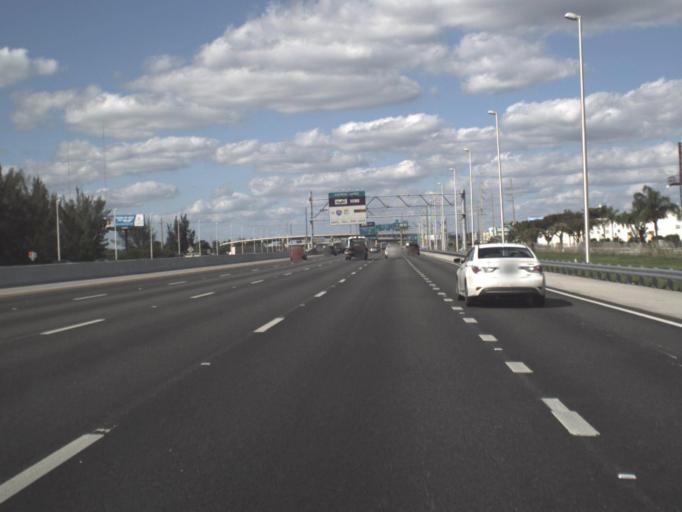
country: US
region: Florida
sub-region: Broward County
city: Davie
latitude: 26.0742
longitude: -80.2156
